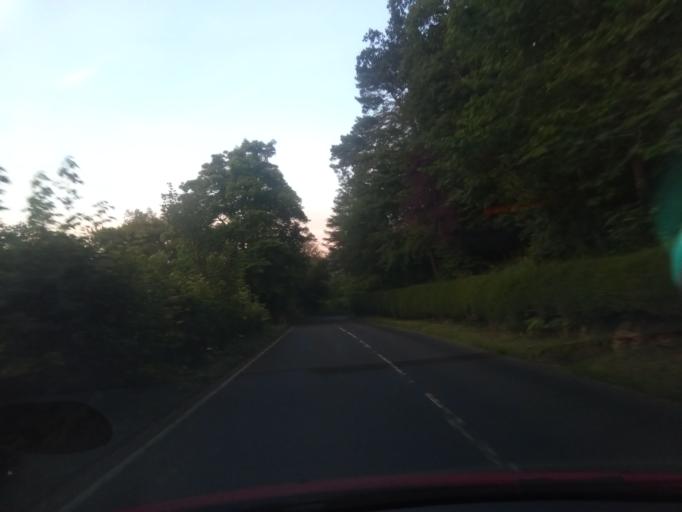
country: GB
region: England
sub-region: Northumberland
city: Bardon Mill
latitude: 54.9043
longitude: -2.3502
